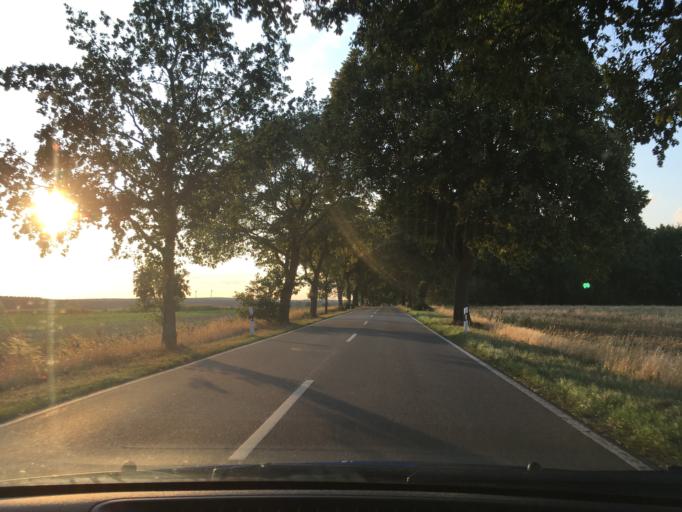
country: DE
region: Lower Saxony
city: Dahlem
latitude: 53.2472
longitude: 10.7761
